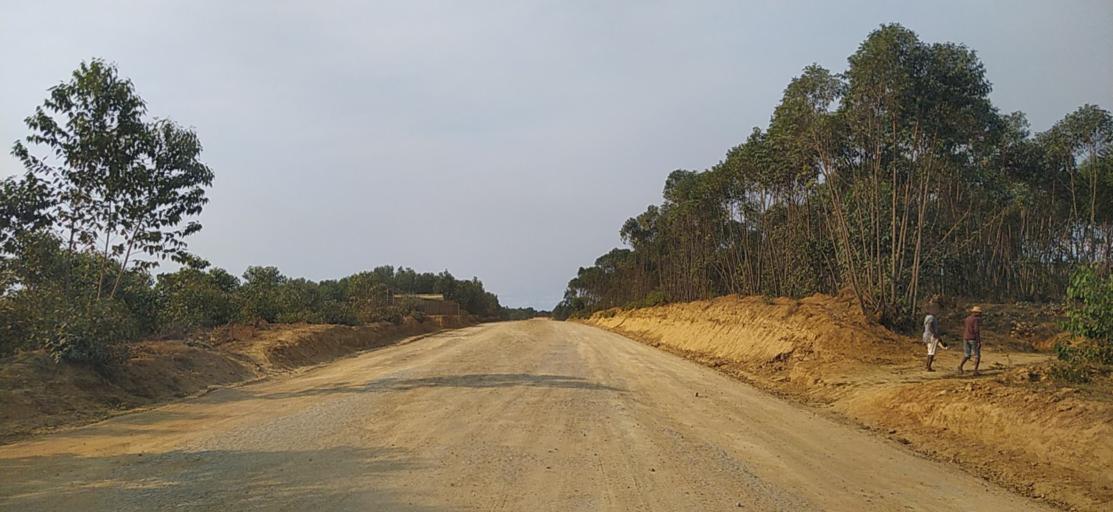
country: MG
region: Alaotra Mangoro
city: Moramanga
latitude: -18.6615
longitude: 48.2738
